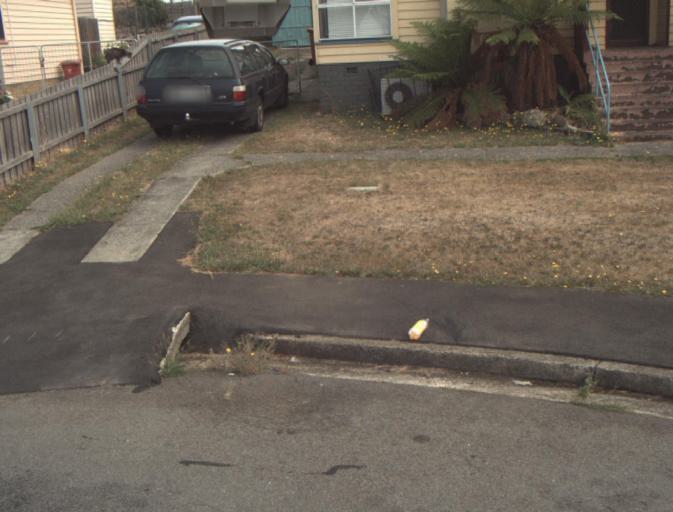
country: AU
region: Tasmania
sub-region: Launceston
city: Mayfield
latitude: -41.3821
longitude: 147.1314
